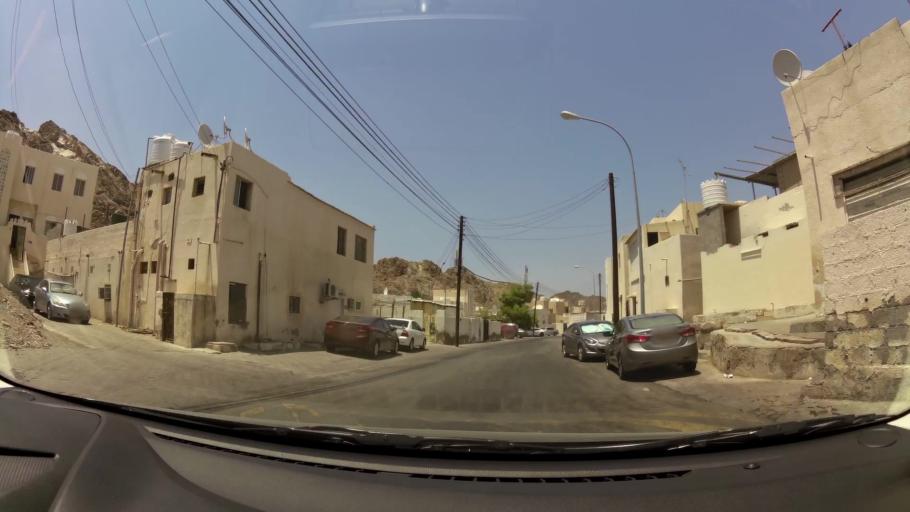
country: OM
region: Muhafazat Masqat
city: Muscat
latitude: 23.6196
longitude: 58.5544
